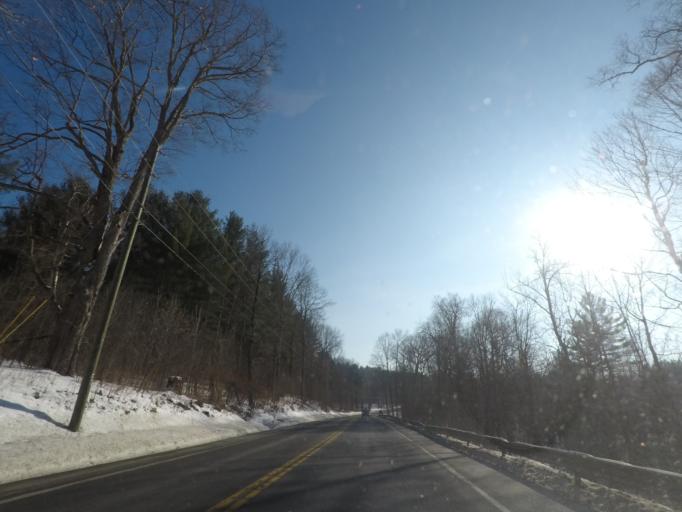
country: US
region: Massachusetts
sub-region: Berkshire County
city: Richmond
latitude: 42.5059
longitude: -73.3674
